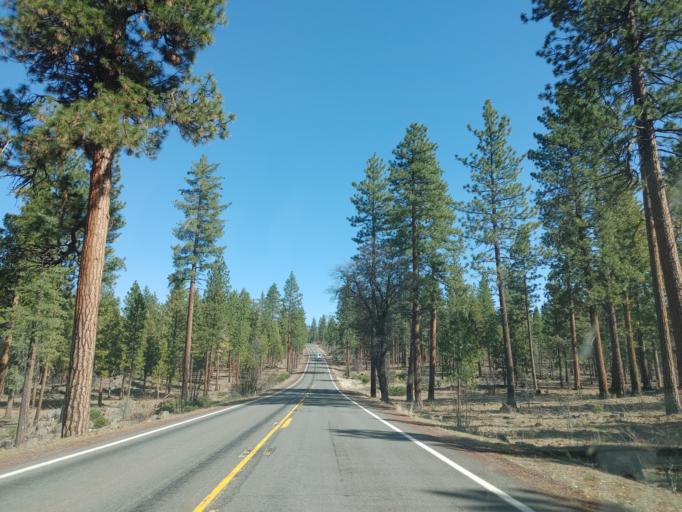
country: US
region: California
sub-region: Shasta County
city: Burney
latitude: 40.7348
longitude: -121.4506
